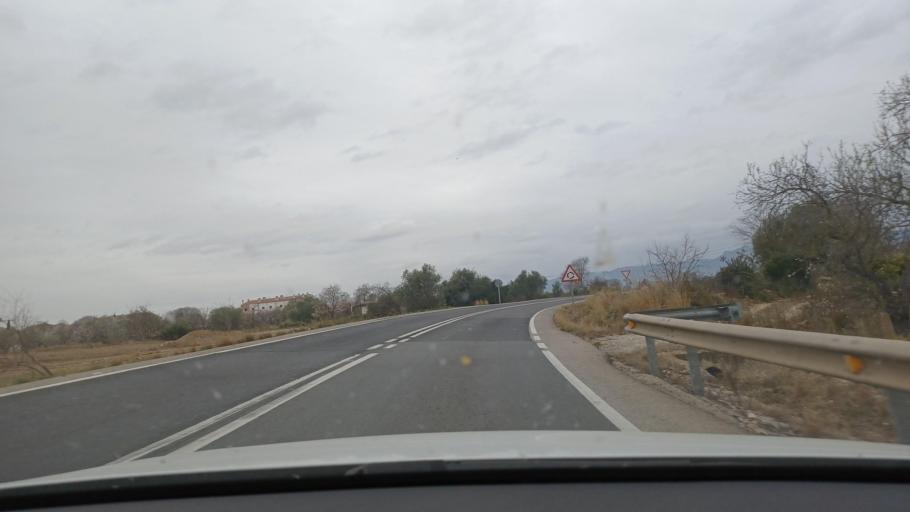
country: ES
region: Catalonia
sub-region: Provincia de Tarragona
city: Santa Barbara
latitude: 40.6857
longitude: 0.4676
